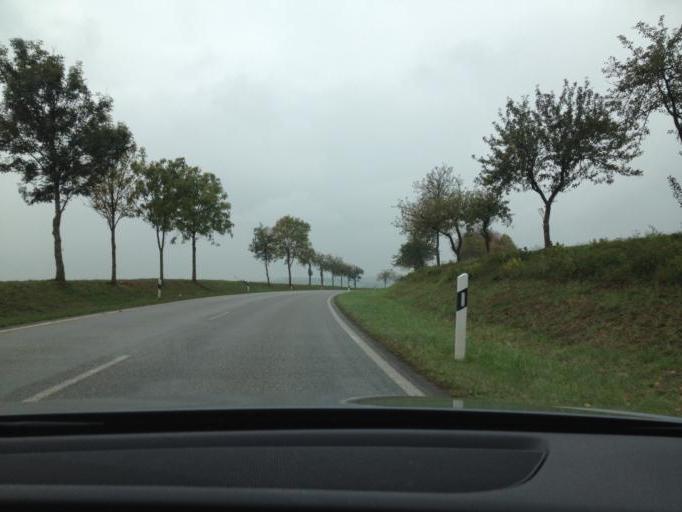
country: DE
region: Baden-Wuerttemberg
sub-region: Regierungsbezirk Stuttgart
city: Bad Rappenau
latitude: 49.2159
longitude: 9.1116
